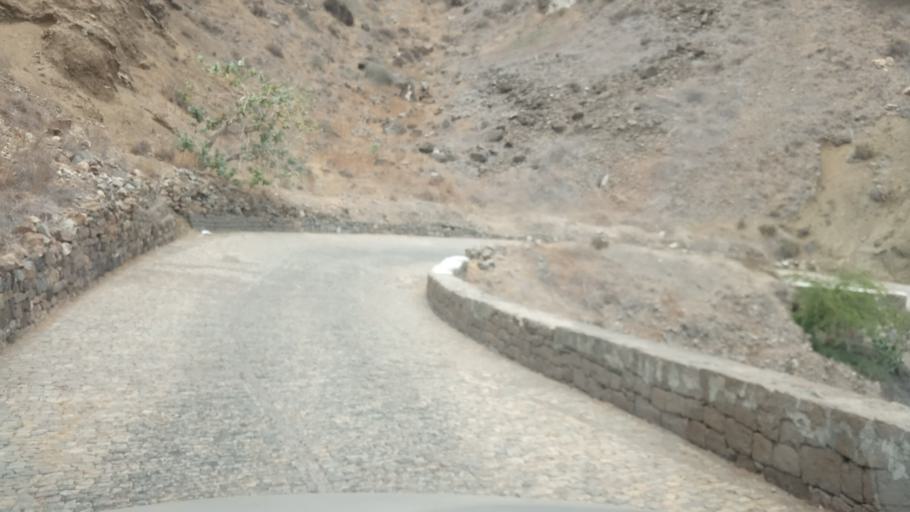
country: CV
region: Brava
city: Vila Nova Sintra
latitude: 14.8765
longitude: -24.7332
